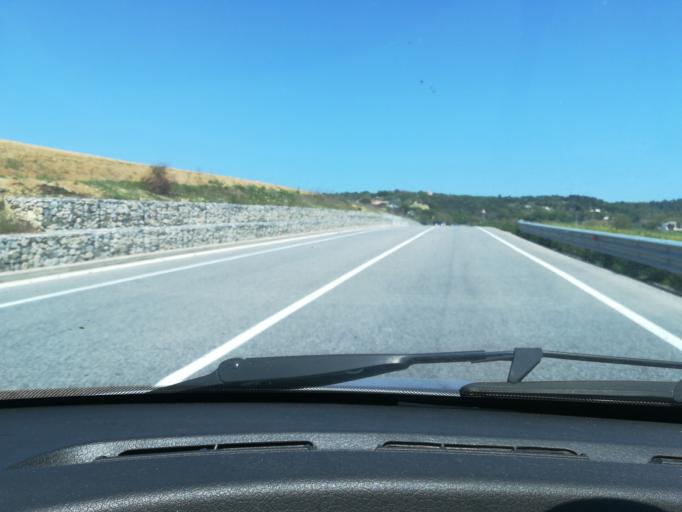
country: IT
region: The Marches
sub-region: Provincia di Ancona
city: Villa Musone
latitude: 43.4548
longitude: 13.5809
